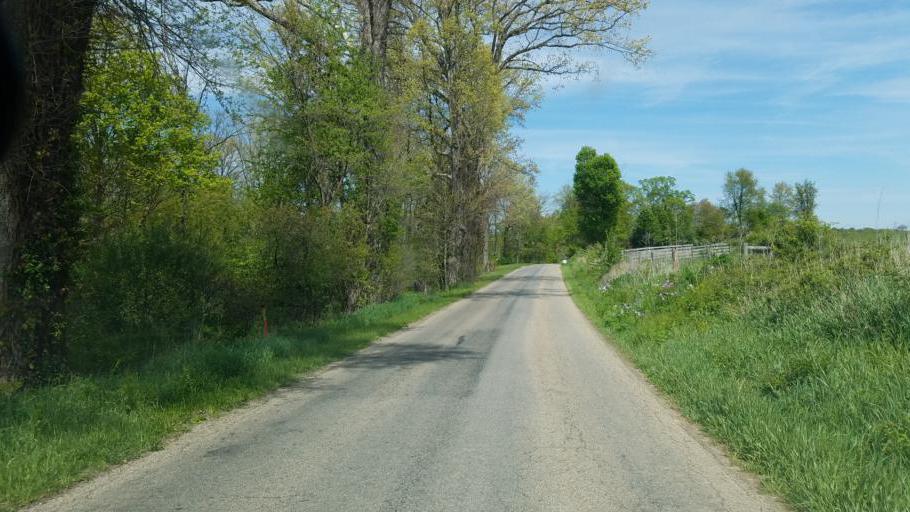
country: US
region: Ohio
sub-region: Knox County
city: Gambier
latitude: 40.4217
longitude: -82.3941
